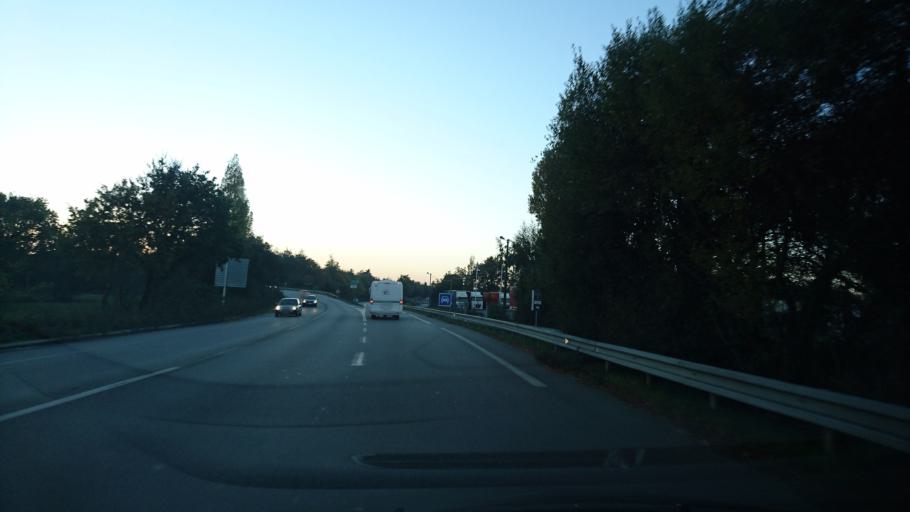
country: FR
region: Brittany
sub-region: Departement du Morbihan
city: Auray
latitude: 47.6831
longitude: -3.0198
